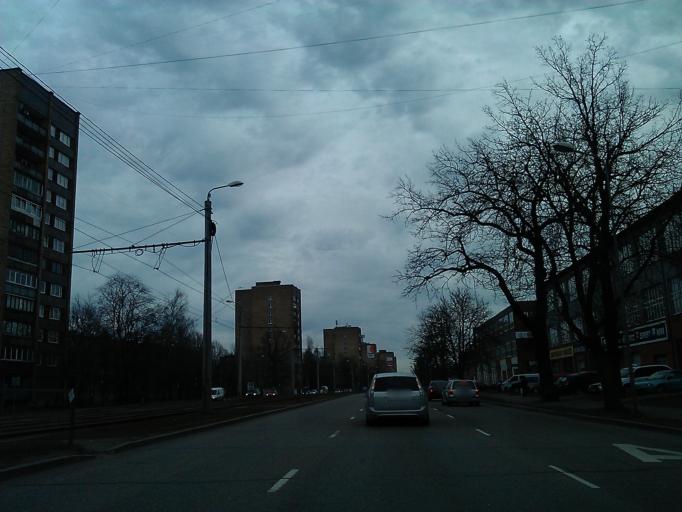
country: LV
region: Kekava
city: Balozi
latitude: 56.9204
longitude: 24.1716
